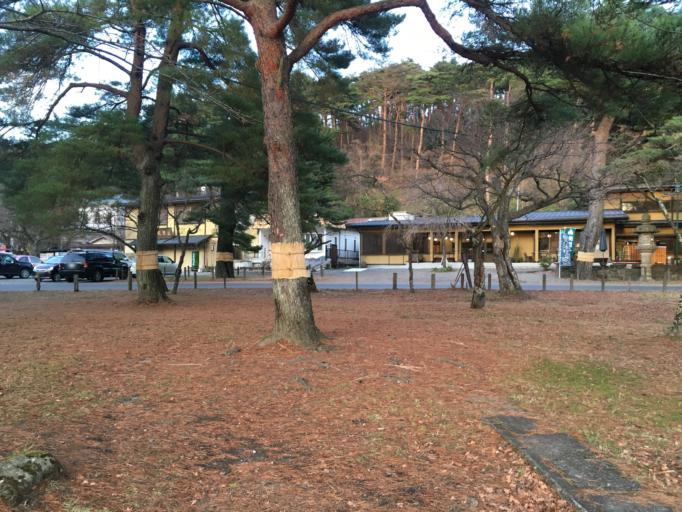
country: JP
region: Tochigi
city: Kuroiso
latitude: 37.1108
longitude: 140.2188
